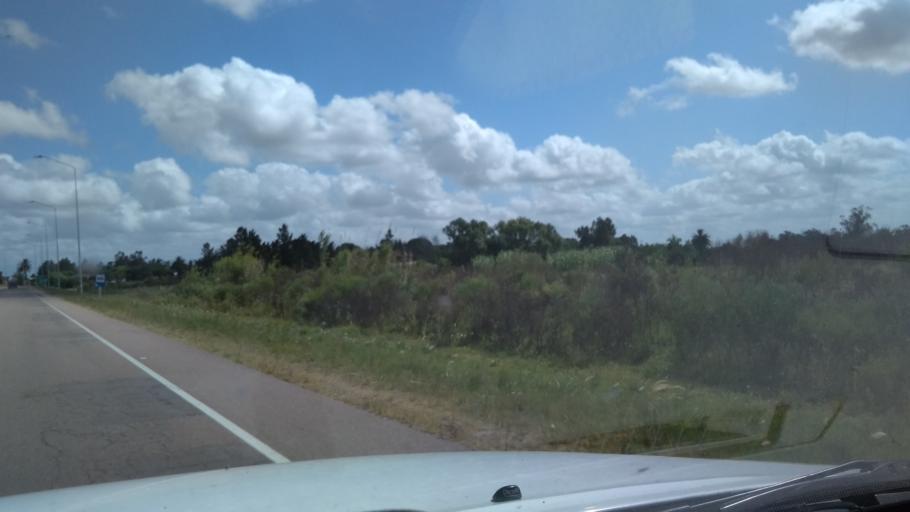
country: UY
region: Canelones
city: Sauce
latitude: -34.6608
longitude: -56.0566
